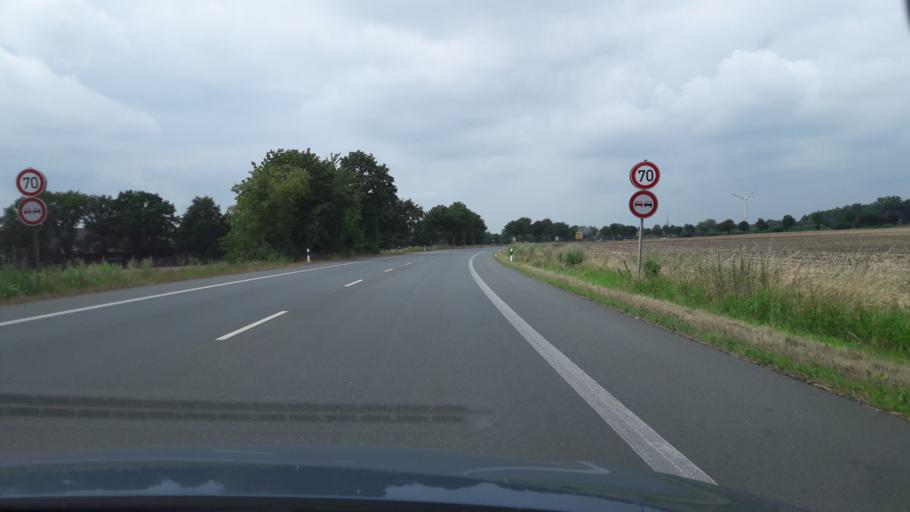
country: DE
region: North Rhine-Westphalia
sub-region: Regierungsbezirk Munster
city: Telgte
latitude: 51.9282
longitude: 7.7613
